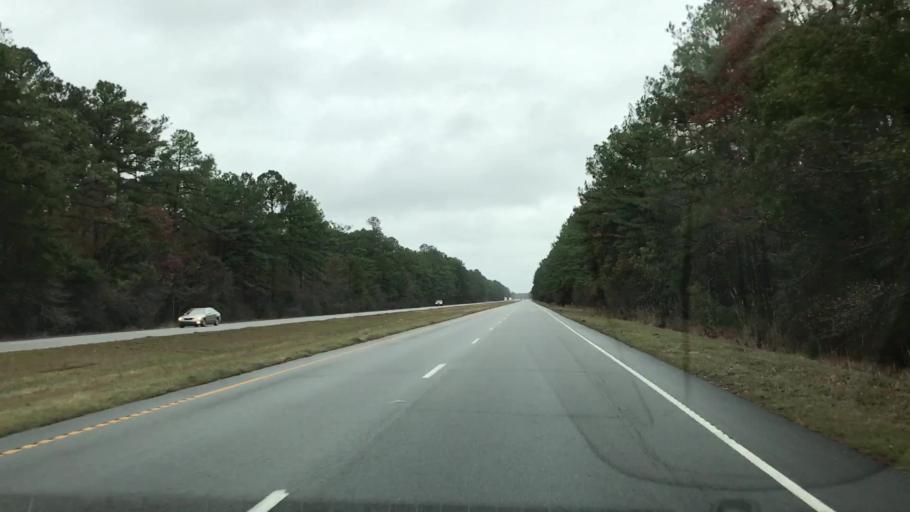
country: US
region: South Carolina
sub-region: Charleston County
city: Awendaw
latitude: 33.1569
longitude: -79.4286
